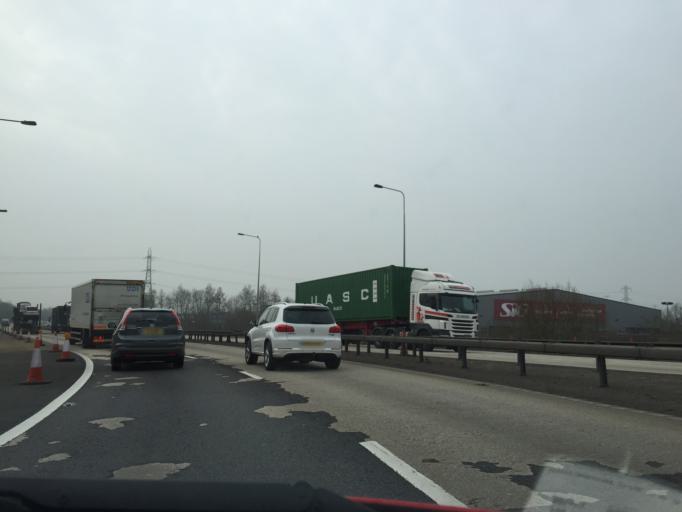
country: GB
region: England
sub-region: Hampshire
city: Totton
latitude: 50.9447
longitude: -1.4755
